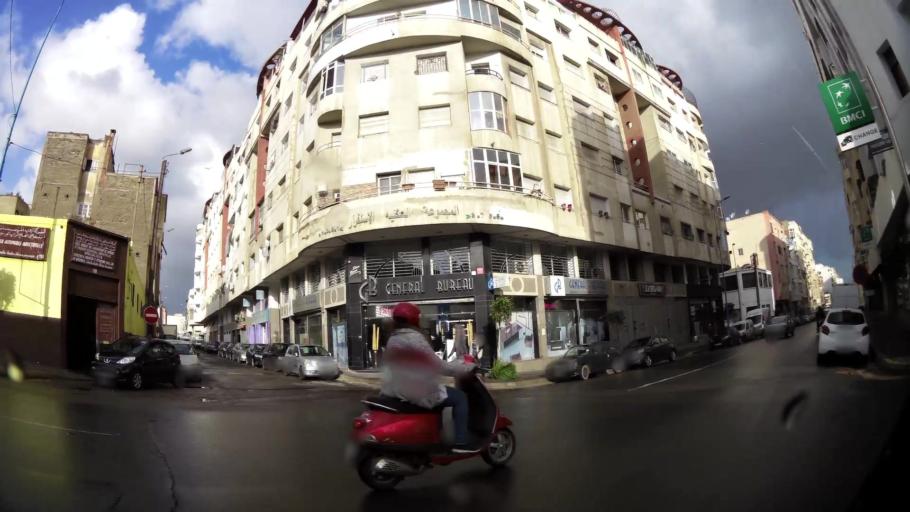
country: MA
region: Grand Casablanca
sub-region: Casablanca
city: Casablanca
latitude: 33.5852
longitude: -7.6003
